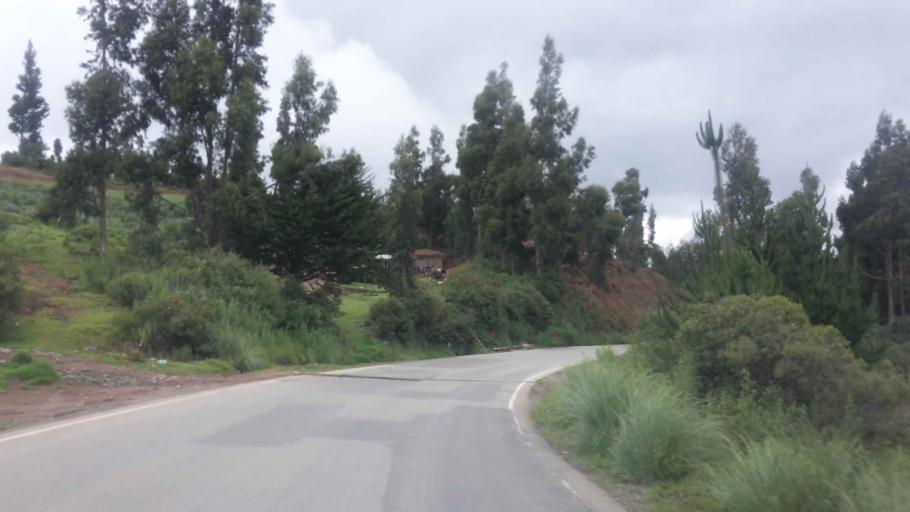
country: BO
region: Cochabamba
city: Totora
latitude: -17.5701
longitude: -65.3176
